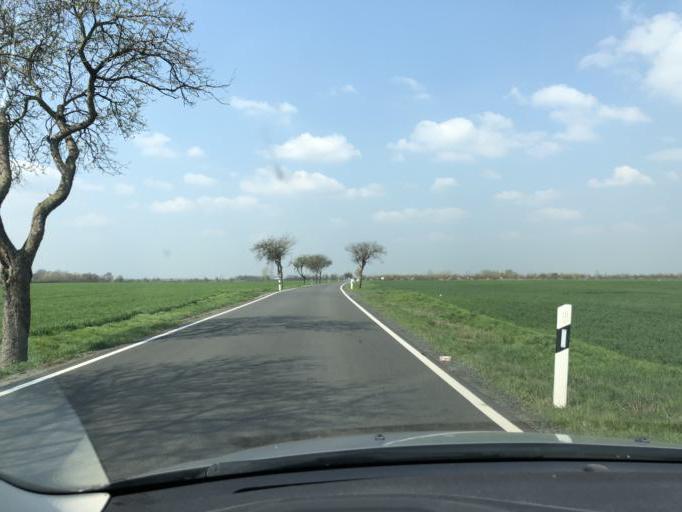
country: DE
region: Saxony
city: Wiedemar
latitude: 51.4907
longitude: 12.2147
